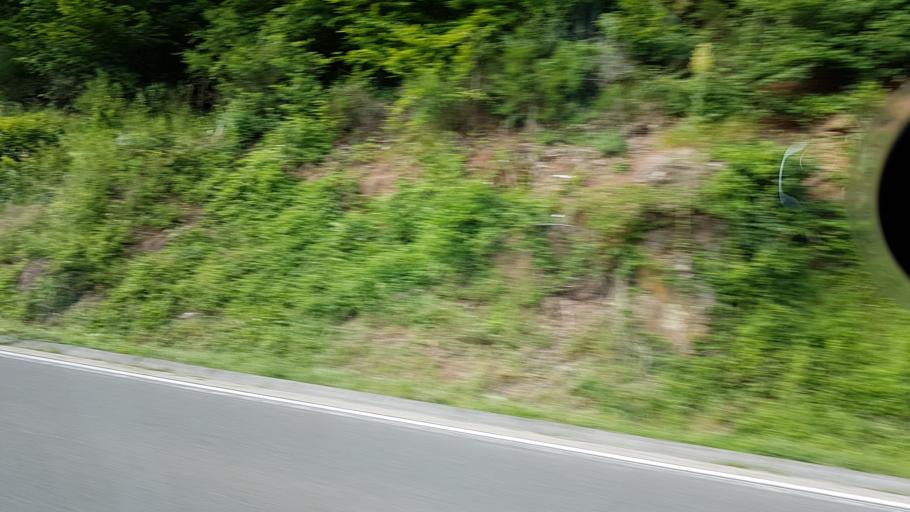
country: DE
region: Rheinland-Pfalz
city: Ulmet
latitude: 49.6088
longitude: 7.4354
